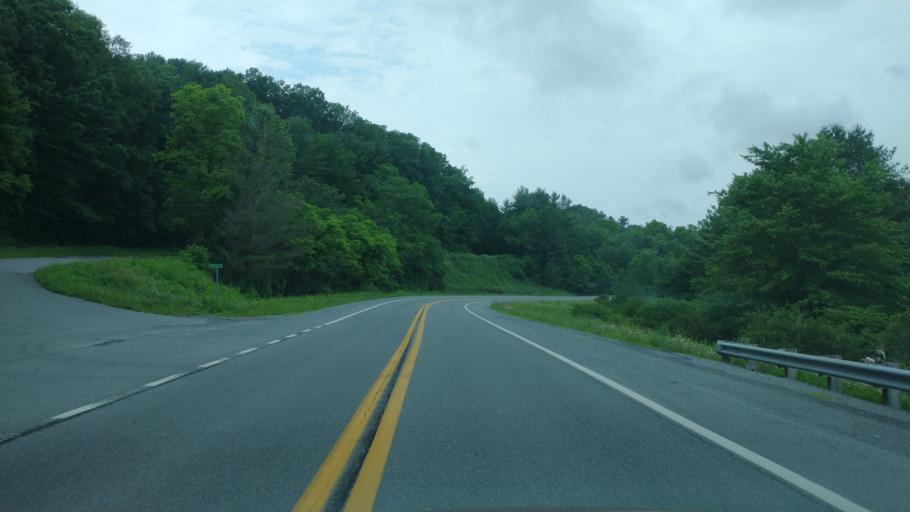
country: US
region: West Virginia
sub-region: Mercer County
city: Athens
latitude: 37.4172
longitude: -81.0576
